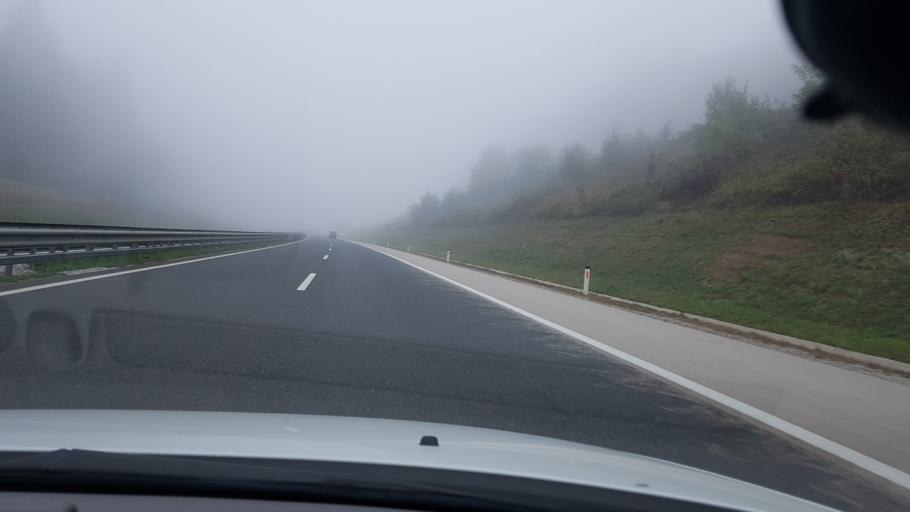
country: SI
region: Mirna Pec
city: Mirna Pec
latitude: 45.8866
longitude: 15.0696
